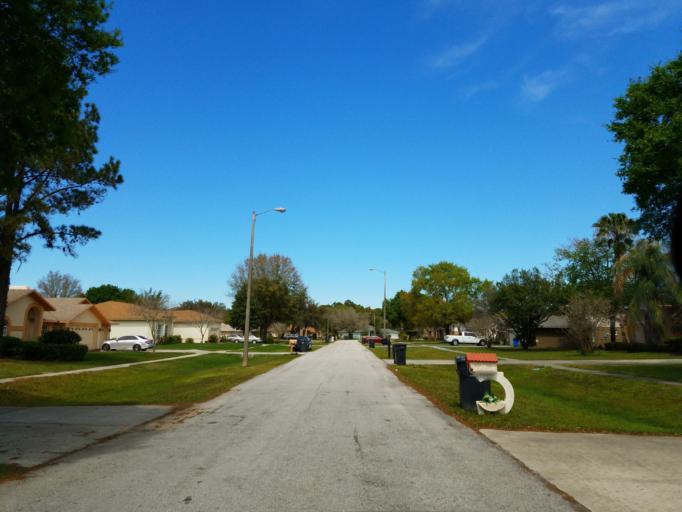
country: US
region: Florida
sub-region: Hillsborough County
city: Thonotosassa
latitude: 28.0662
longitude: -82.3104
